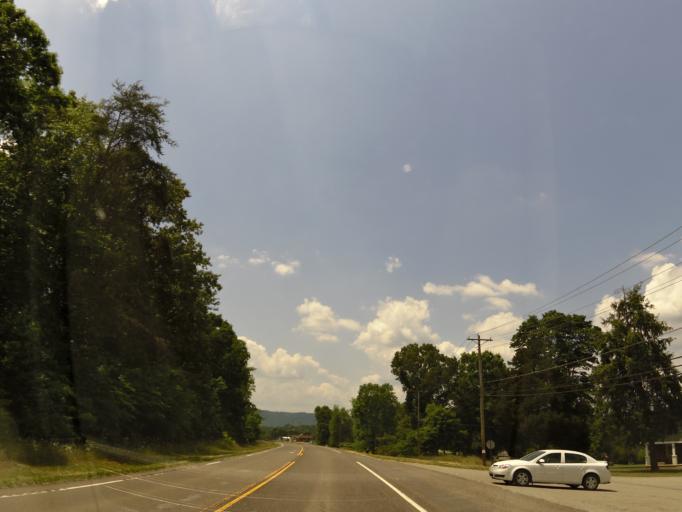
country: US
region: Tennessee
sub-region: Rhea County
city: Spring City
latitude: 35.6440
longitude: -84.8479
